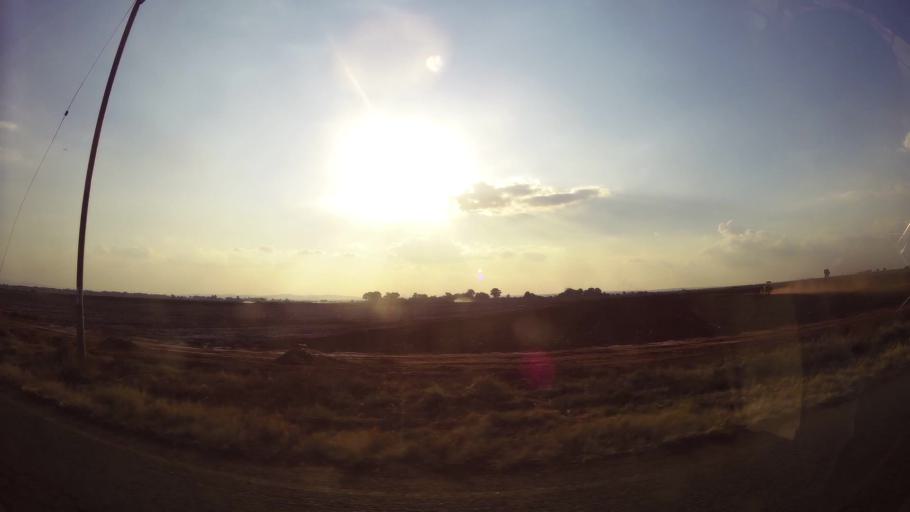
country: ZA
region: Gauteng
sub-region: Ekurhuleni Metropolitan Municipality
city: Germiston
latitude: -26.3234
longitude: 28.2437
